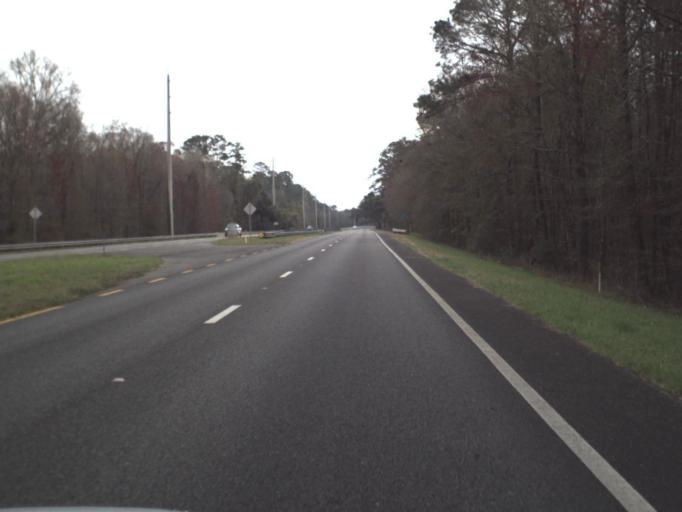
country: US
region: Florida
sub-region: Leon County
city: Tallahassee
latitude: 30.4211
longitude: -84.1037
